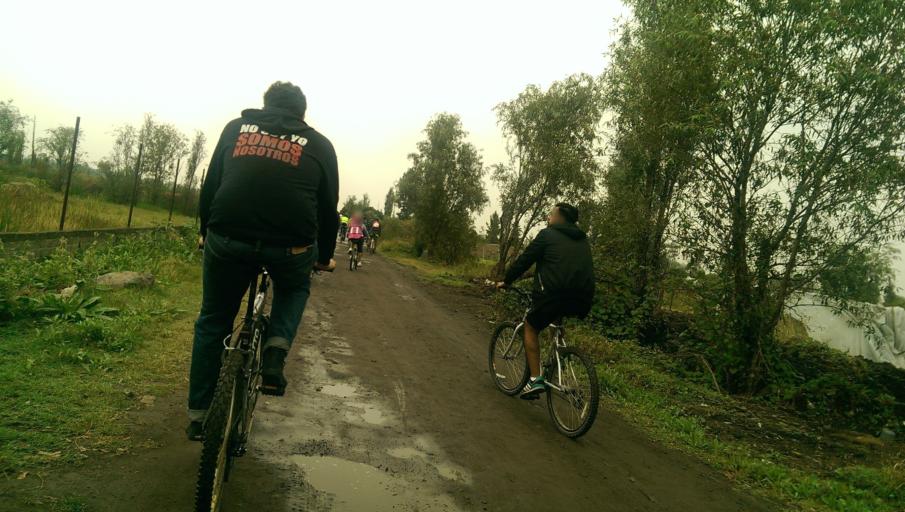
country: MX
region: Mexico City
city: Xochimilco
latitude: 19.2656
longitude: -99.0749
